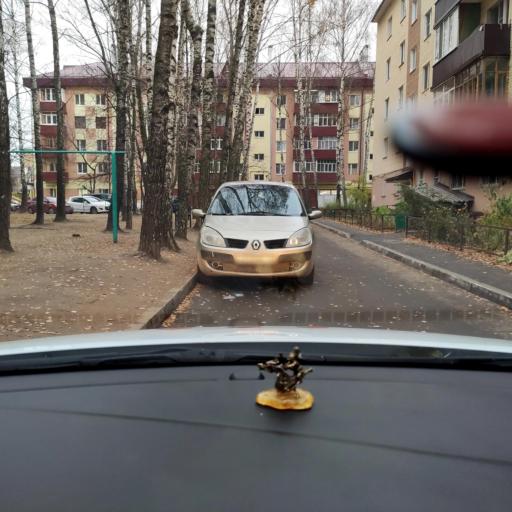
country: RU
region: Tatarstan
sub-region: Zelenodol'skiy Rayon
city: Zelenodolsk
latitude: 55.8500
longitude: 48.5595
